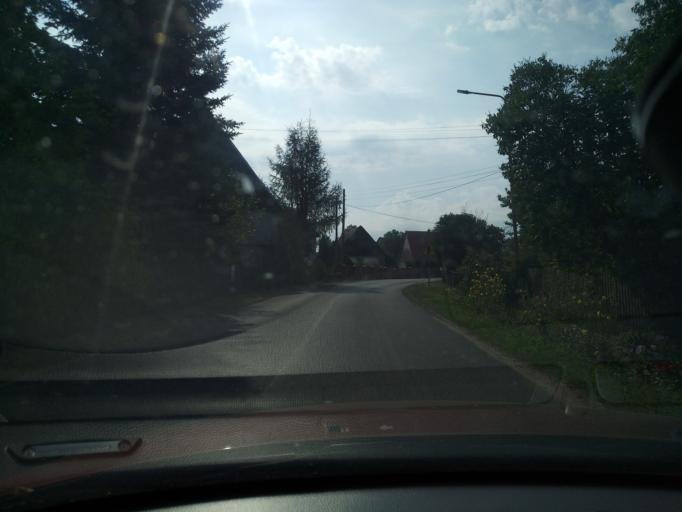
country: PL
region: Lower Silesian Voivodeship
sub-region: Powiat jeleniogorski
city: Stara Kamienica
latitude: 50.9011
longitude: 15.5722
